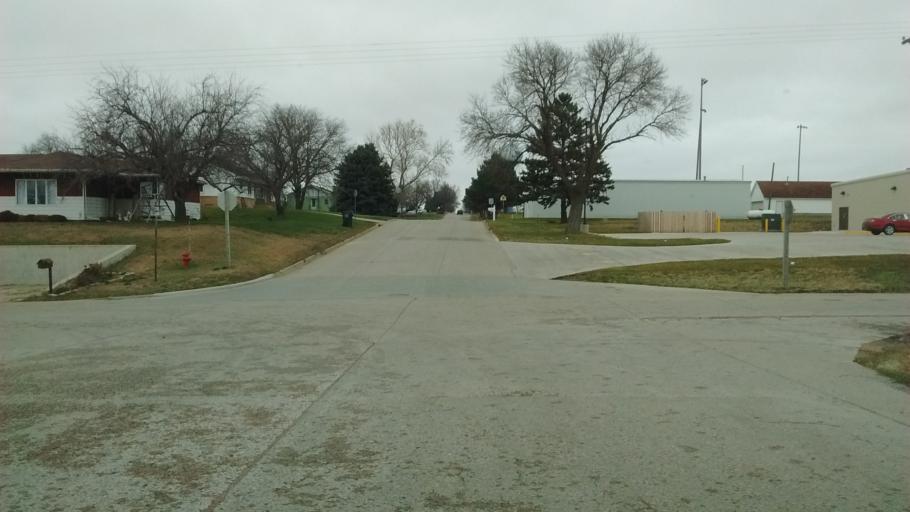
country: US
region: Iowa
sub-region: Woodbury County
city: Moville
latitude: 42.4819
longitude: -96.0653
